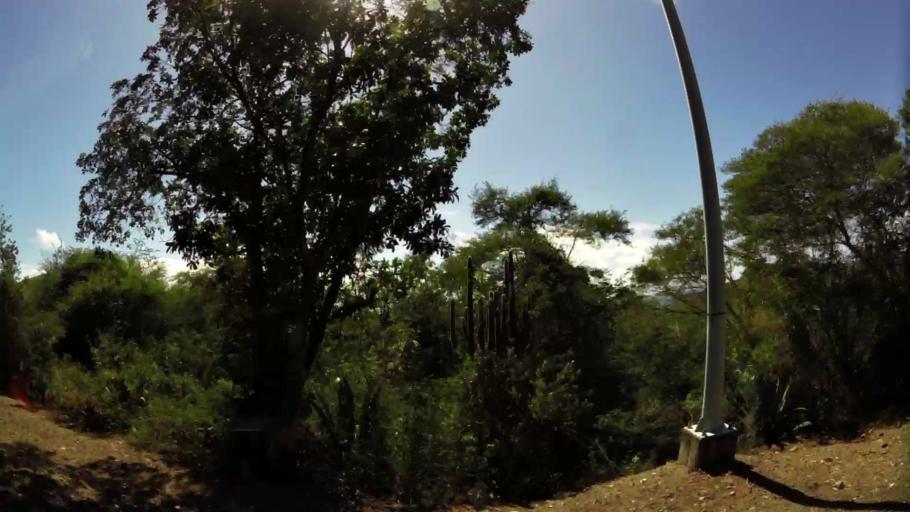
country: AG
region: Saint Paul
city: Falmouth
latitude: 17.0102
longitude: -61.7585
